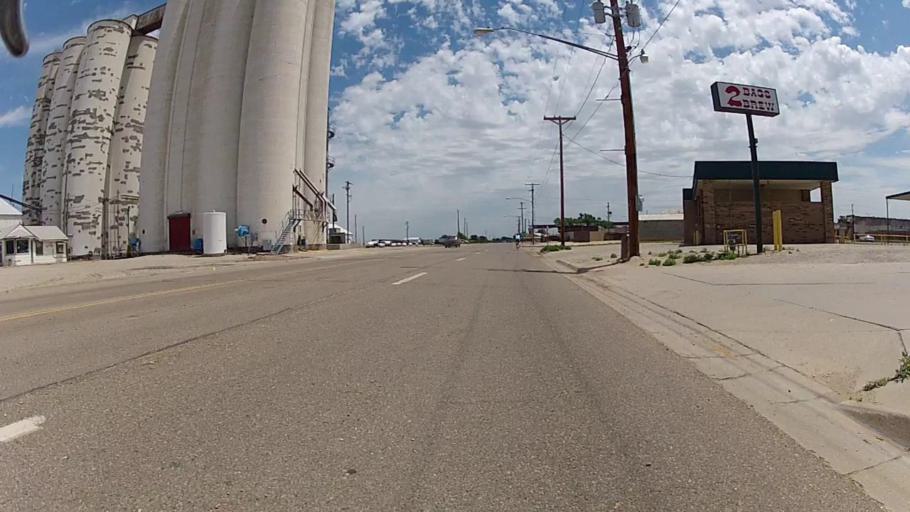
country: US
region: Kansas
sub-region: Haskell County
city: Satanta
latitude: 37.4399
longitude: -100.9874
